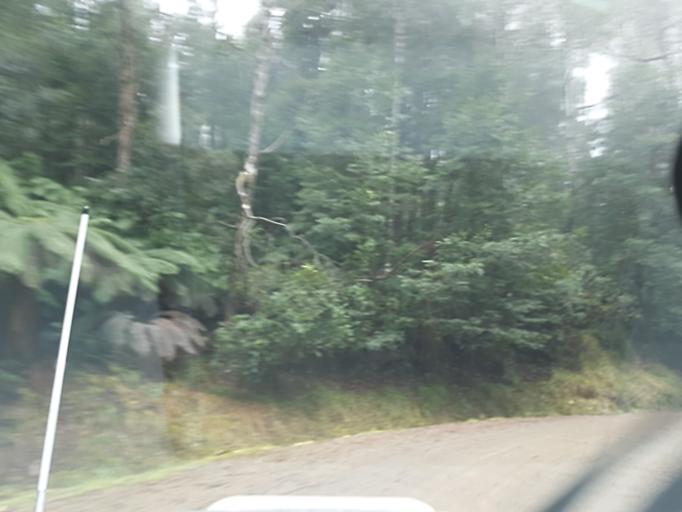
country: AU
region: Victoria
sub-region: Yarra Ranges
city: Millgrove
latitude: -37.5462
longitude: 145.8939
